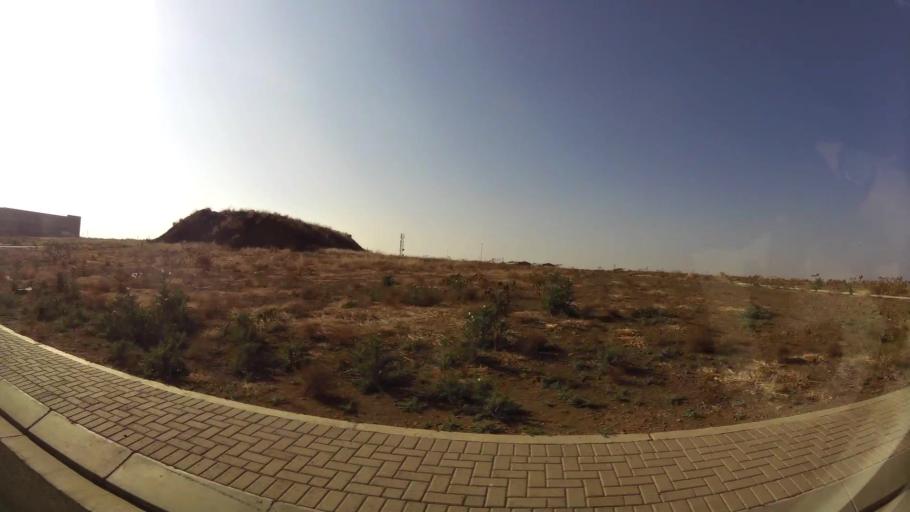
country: ZA
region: Orange Free State
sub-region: Mangaung Metropolitan Municipality
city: Bloemfontein
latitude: -29.1877
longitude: 26.2167
